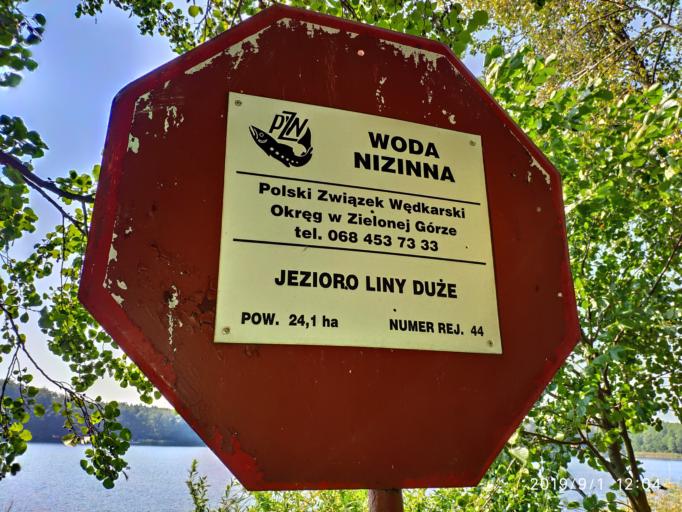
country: PL
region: Lubusz
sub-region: Powiat zielonogorski
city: Kargowa
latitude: 52.1114
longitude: 15.8303
